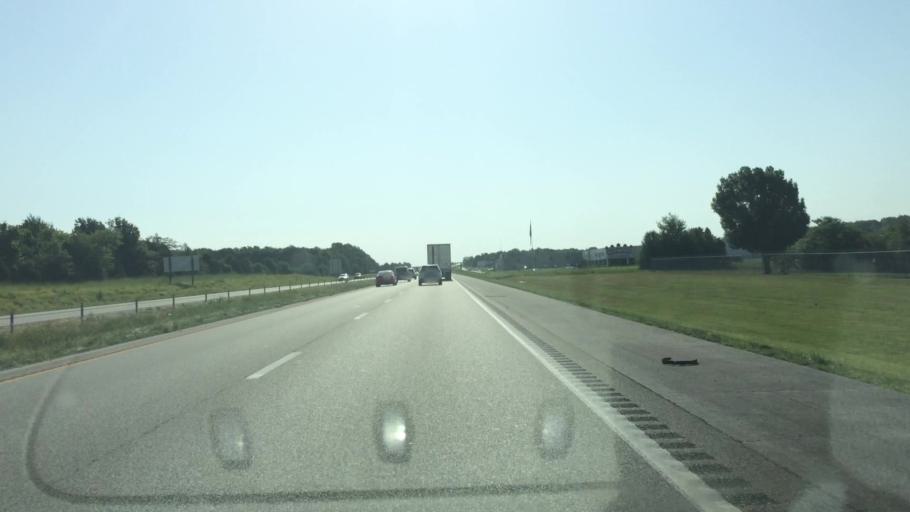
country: US
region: Missouri
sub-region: Greene County
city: Strafford
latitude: 37.2501
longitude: -93.2039
